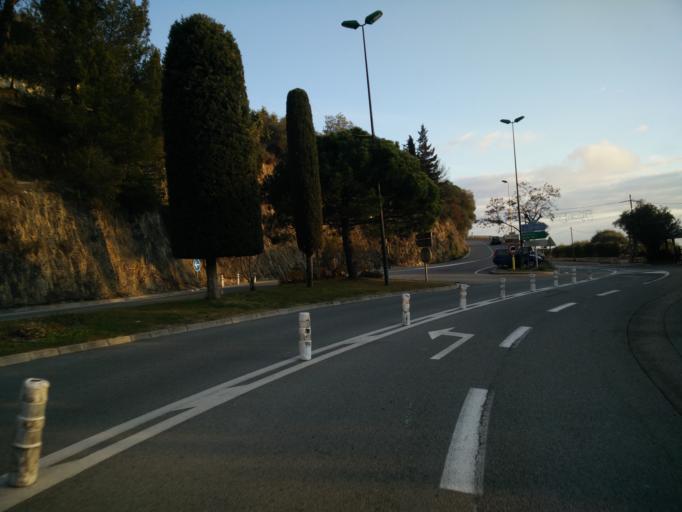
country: FR
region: Provence-Alpes-Cote d'Azur
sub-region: Departement des Alpes-Maritimes
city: Eze
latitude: 43.7301
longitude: 7.3664
